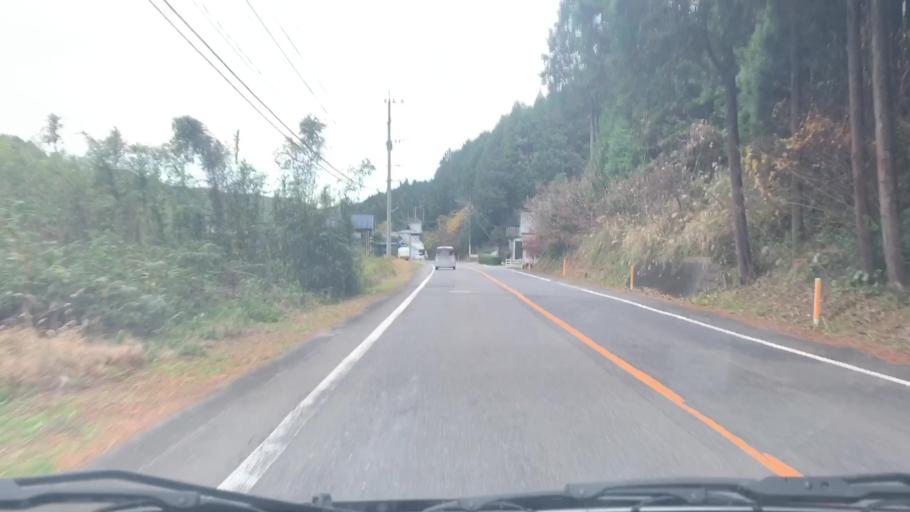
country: JP
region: Saga Prefecture
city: Takeocho-takeo
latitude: 33.1865
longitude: 129.9680
